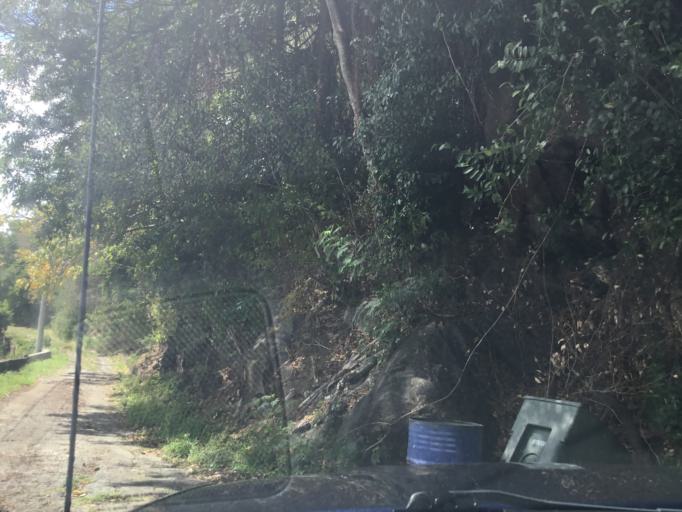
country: VC
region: Saint George
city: Kingstown Park
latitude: 13.1589
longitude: -61.2396
